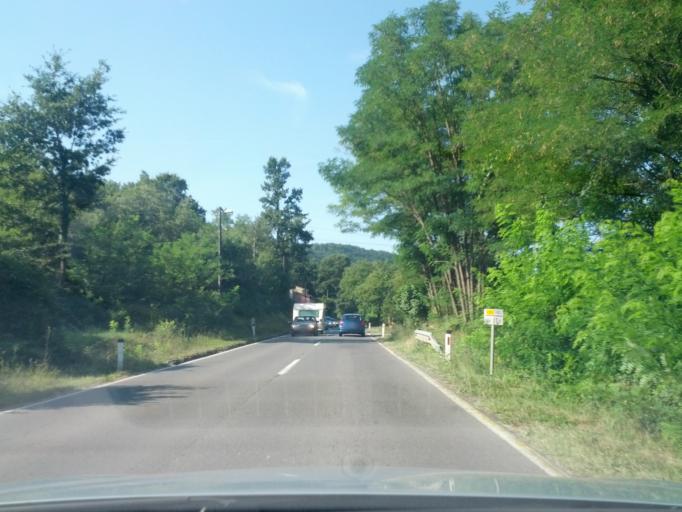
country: SI
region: Izola-Isola
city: Jagodje
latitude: 45.4749
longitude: 13.6746
